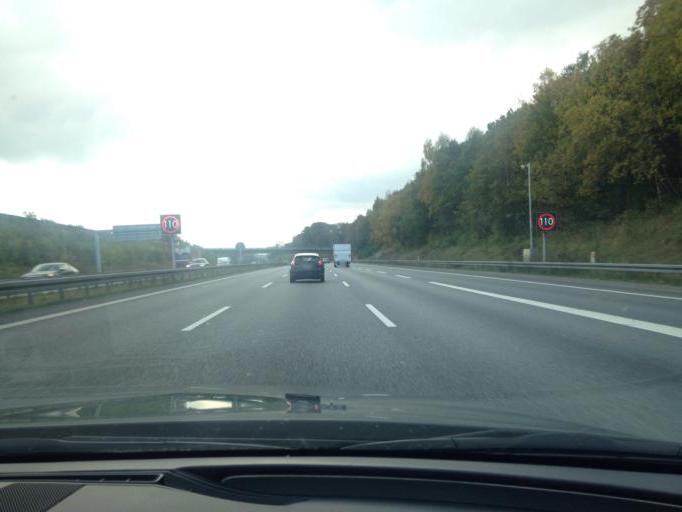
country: DK
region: South Denmark
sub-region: Vejle Kommune
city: Vejle
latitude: 55.7199
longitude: 9.5756
